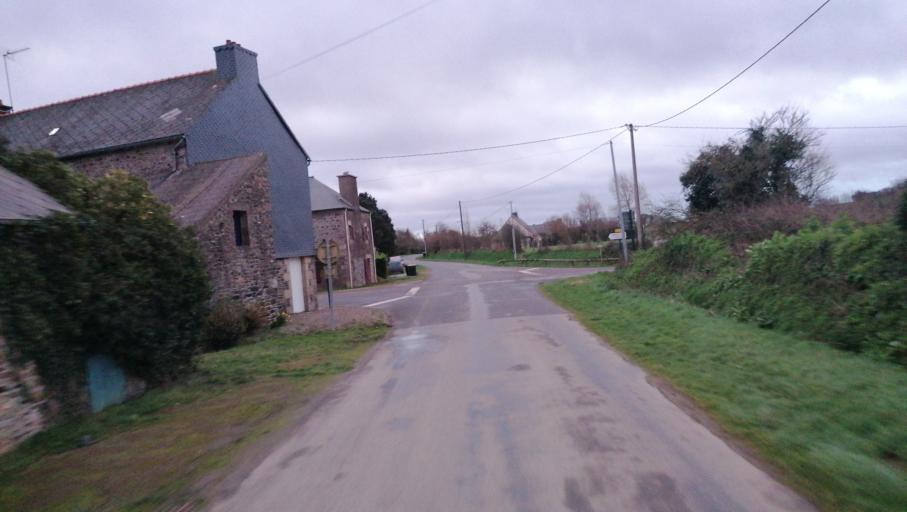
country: FR
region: Brittany
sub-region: Departement des Cotes-d'Armor
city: Plehedel
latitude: 48.6648
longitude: -3.0275
